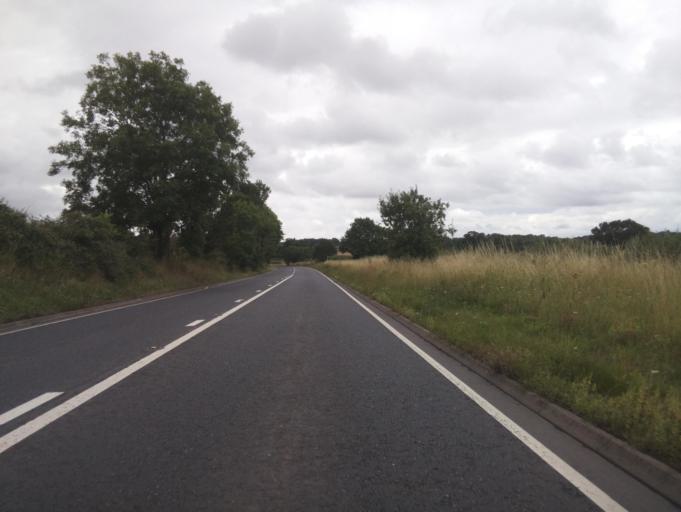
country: GB
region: England
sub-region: Worcestershire
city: Fernhill Heath
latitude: 52.2366
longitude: -2.1731
